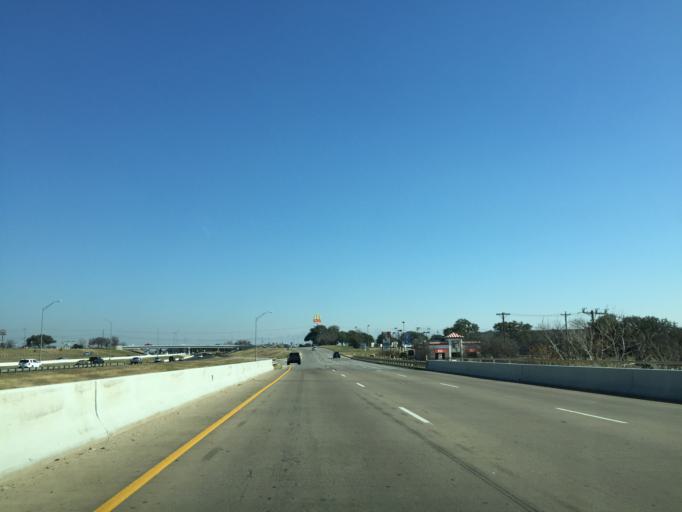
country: US
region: Texas
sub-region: Williamson County
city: Georgetown
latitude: 30.6460
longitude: -97.6825
